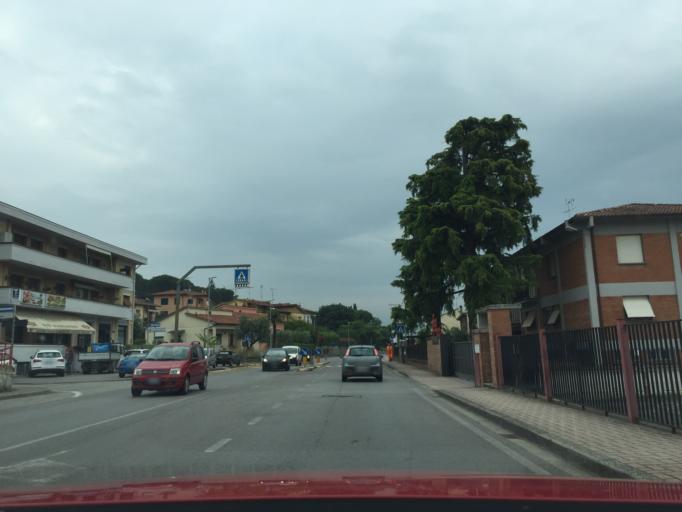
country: IT
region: Tuscany
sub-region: Provincia di Pistoia
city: Stazione Masotti
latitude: 43.9104
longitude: 10.8538
